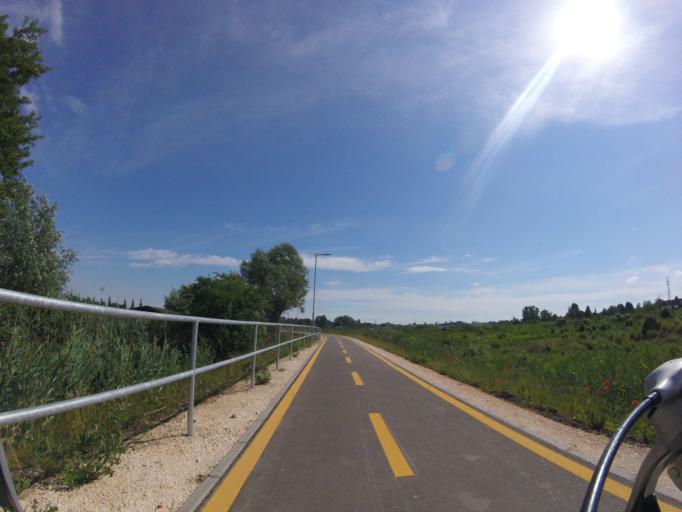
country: HU
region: Fejer
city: Bicske
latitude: 47.5051
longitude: 18.6306
